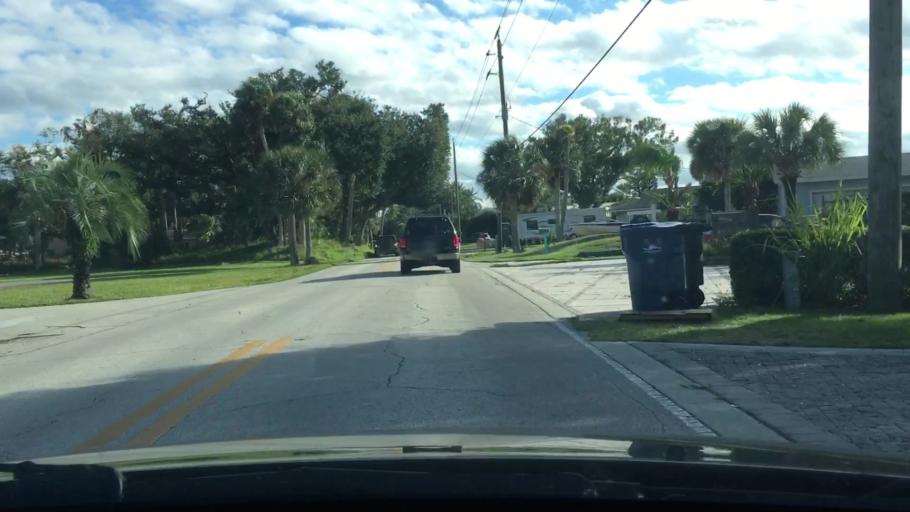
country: US
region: Florida
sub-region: Volusia County
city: Ormond-by-the-Sea
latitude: 29.3216
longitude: -81.0627
